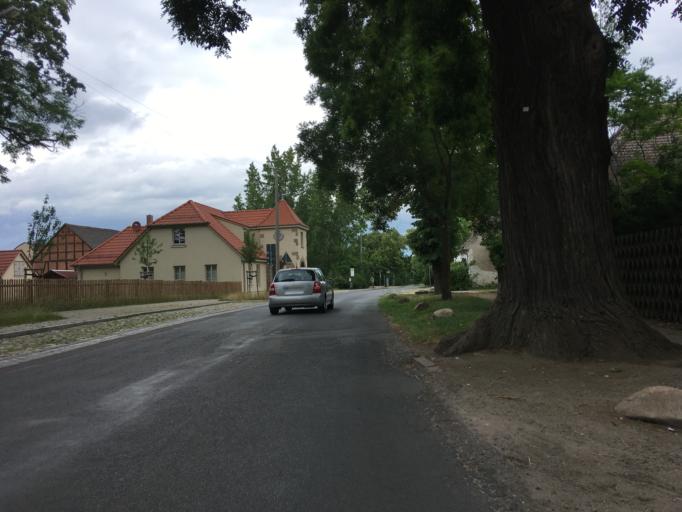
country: DE
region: Saxony-Anhalt
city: Quellendorf
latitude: 51.8047
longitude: 12.1494
